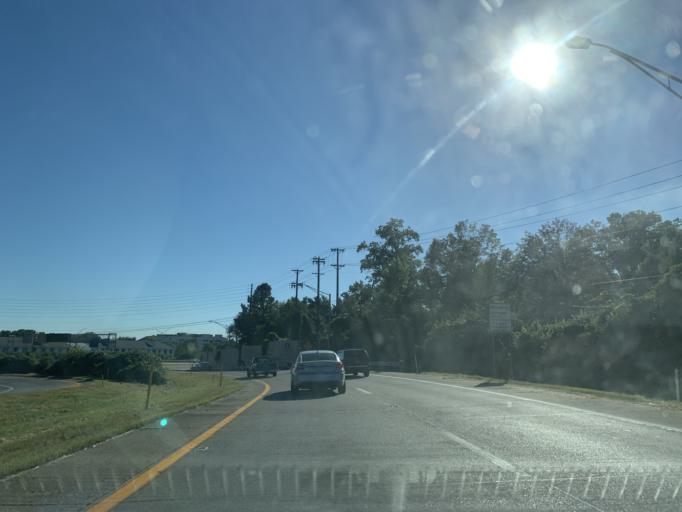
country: US
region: Kentucky
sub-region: Jefferson County
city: West Buechel
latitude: 38.2030
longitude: -85.6912
